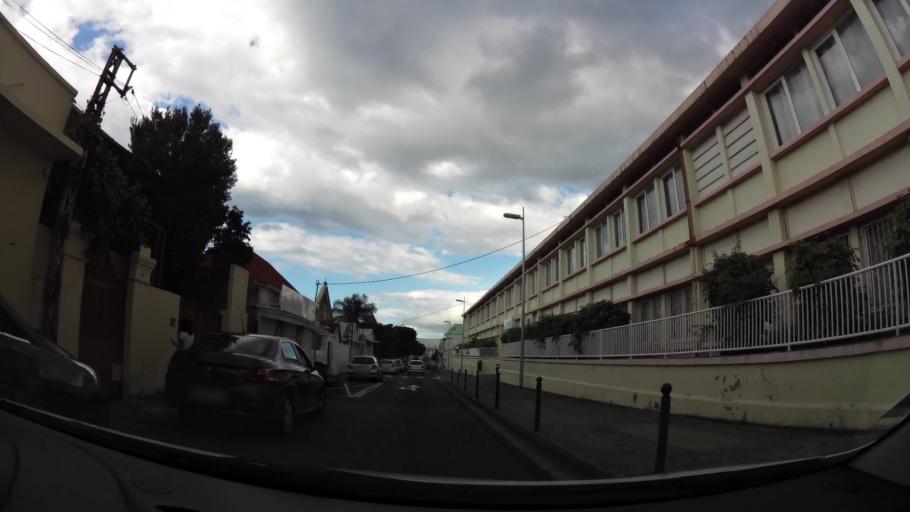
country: RE
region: Reunion
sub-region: Reunion
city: Saint-Denis
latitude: -20.8832
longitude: 55.4564
